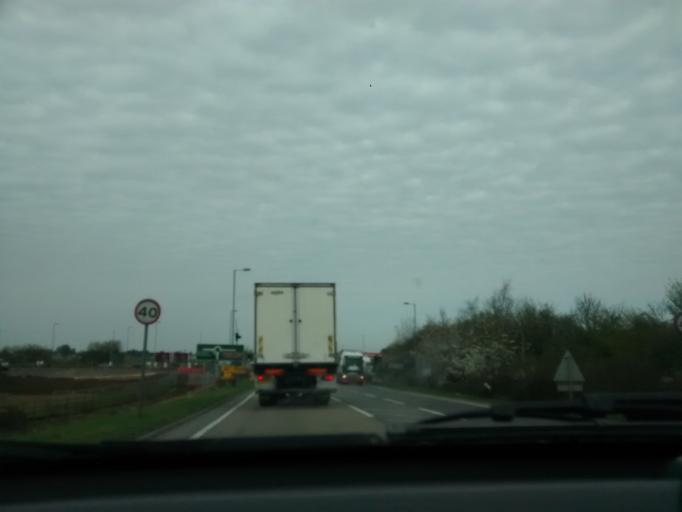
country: GB
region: England
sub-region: Oxfordshire
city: Bicester
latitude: 51.8923
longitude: -1.1599
